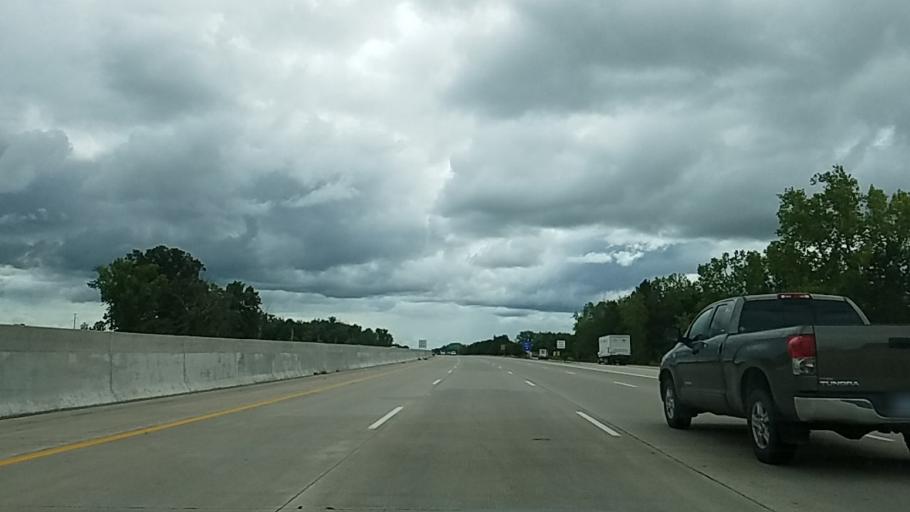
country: US
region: Michigan
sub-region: Saginaw County
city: Zilwaukee
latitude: 43.5329
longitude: -83.9442
